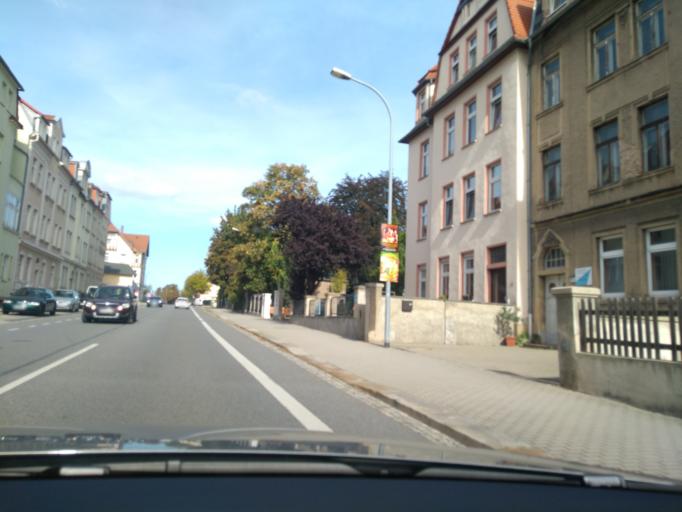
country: DE
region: Saxony
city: Bautzen
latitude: 51.1714
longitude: 14.4340
